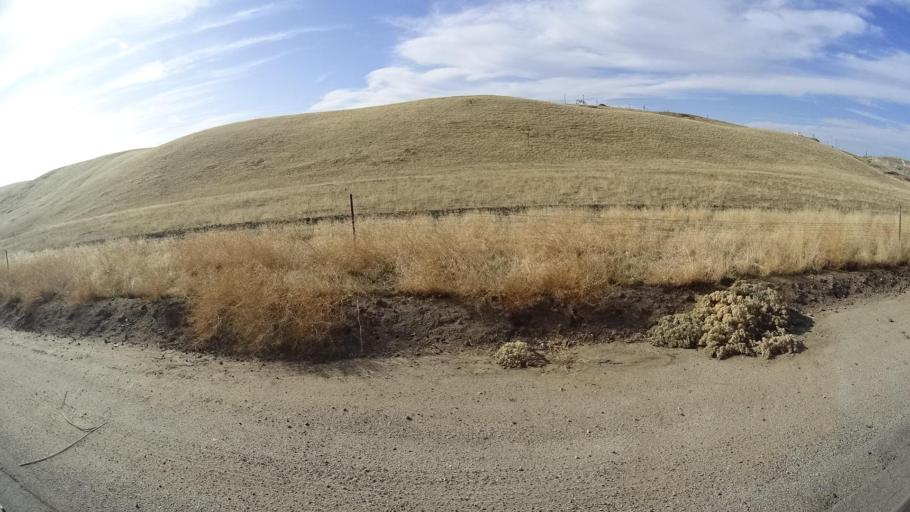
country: US
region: California
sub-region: Kern County
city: Oildale
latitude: 35.6090
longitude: -118.9639
